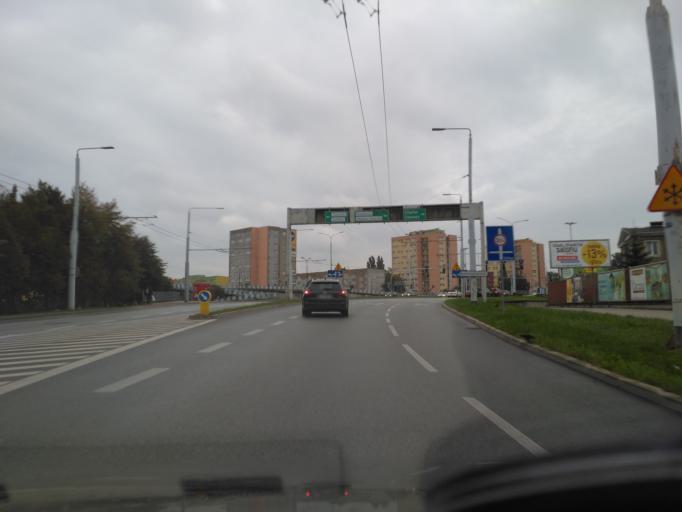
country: PL
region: Lublin Voivodeship
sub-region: Powiat lubelski
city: Lublin
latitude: 51.2424
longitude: 22.5896
